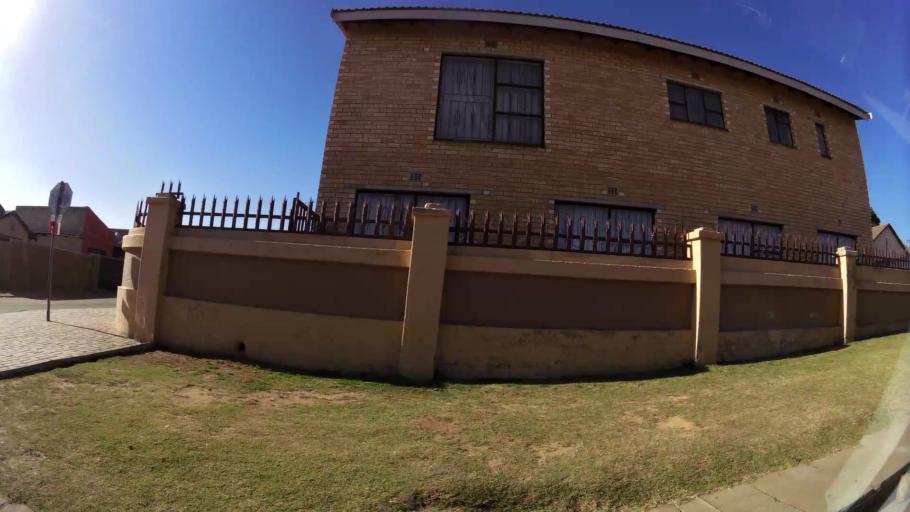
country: ZA
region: Gauteng
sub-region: Ekurhuleni Metropolitan Municipality
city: Tembisa
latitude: -26.0284
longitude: 28.2186
